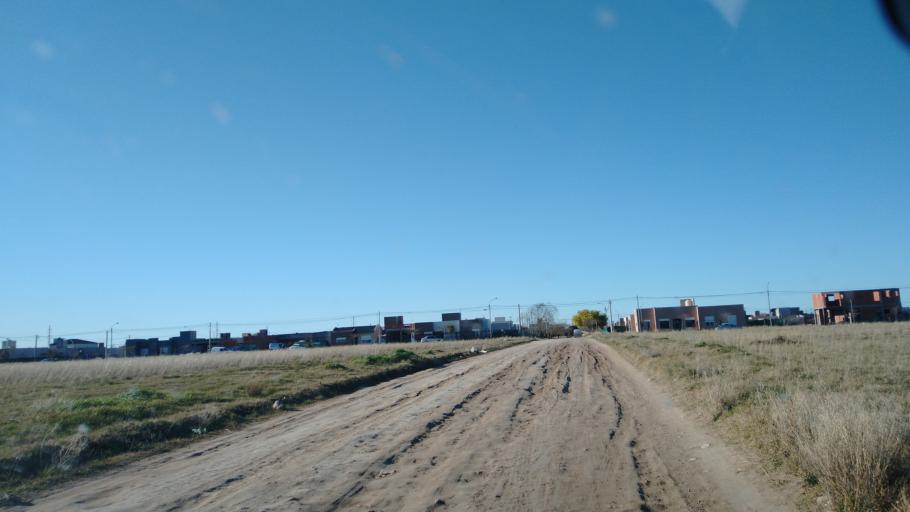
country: AR
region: Buenos Aires
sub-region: Partido de Bahia Blanca
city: Bahia Blanca
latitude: -38.7084
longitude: -62.2057
